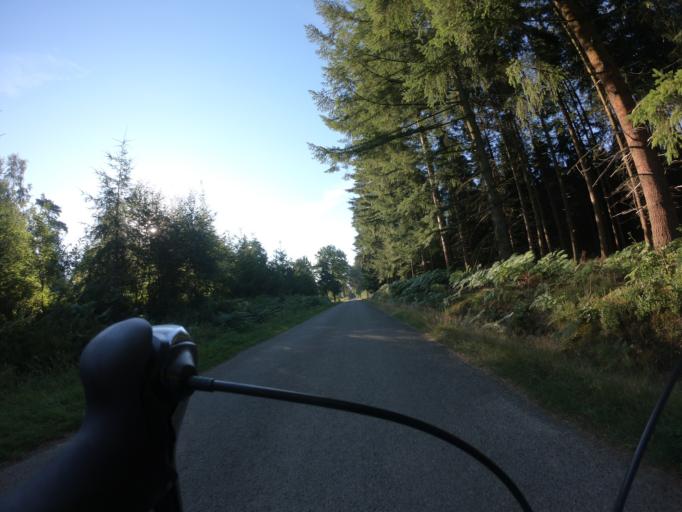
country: FR
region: Lower Normandy
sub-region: Departement de l'Orne
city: Magny-le-Desert
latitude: 48.5351
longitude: -0.2792
